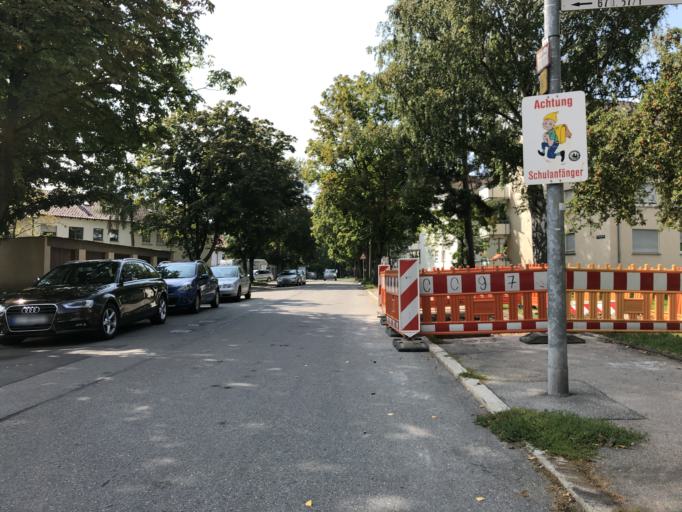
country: DE
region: Baden-Wuerttemberg
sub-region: Regierungsbezirk Stuttgart
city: Sindelfingen
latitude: 48.7271
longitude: 9.0069
